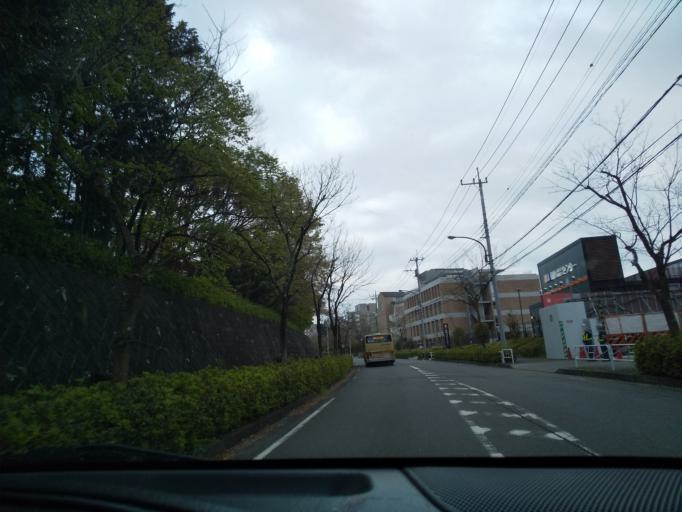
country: JP
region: Tokyo
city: Hino
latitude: 35.6110
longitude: 139.3763
